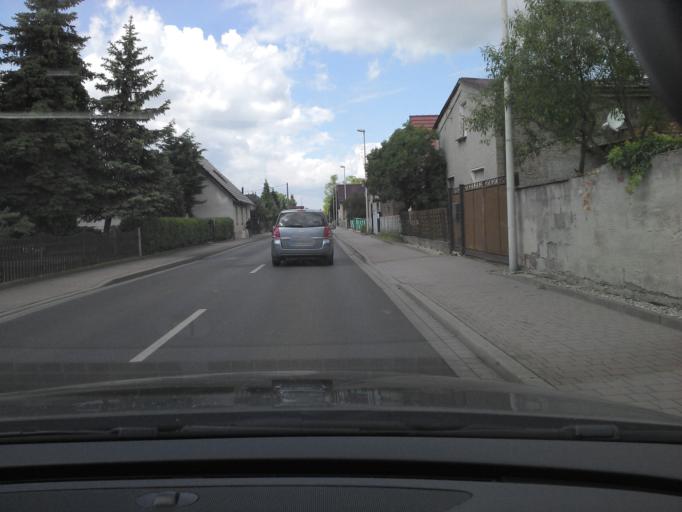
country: DE
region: Brandenburg
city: Werben
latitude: 51.8112
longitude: 14.1903
